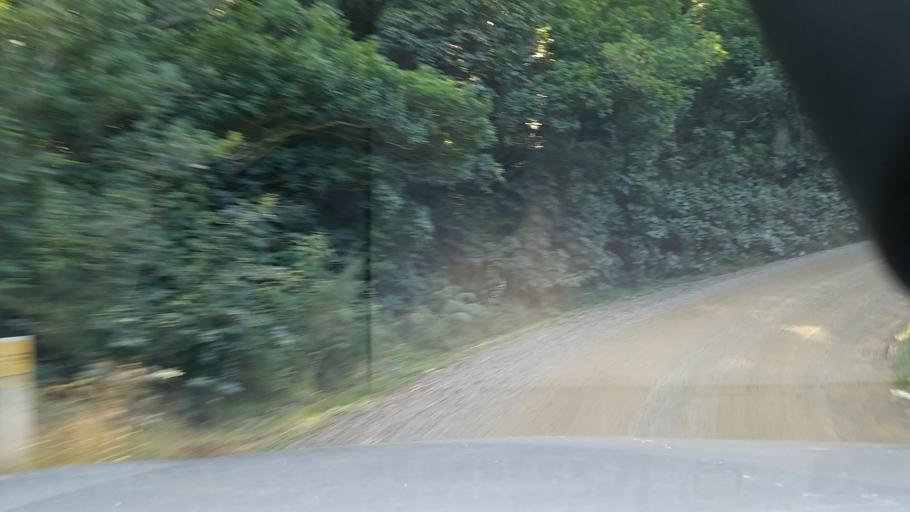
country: NZ
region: Marlborough
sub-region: Marlborough District
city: Picton
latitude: -41.2885
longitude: 174.1715
